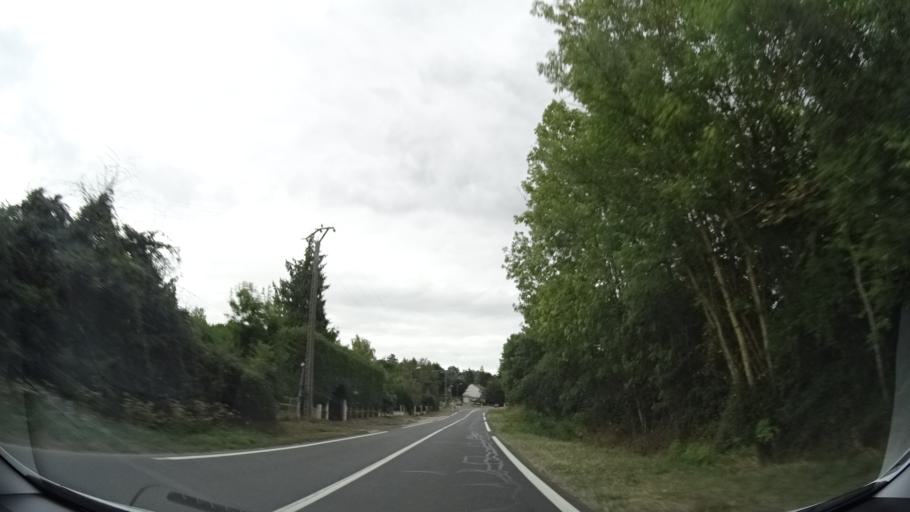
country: FR
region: Centre
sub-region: Departement du Loiret
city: Trigueres
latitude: 47.9385
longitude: 2.9698
